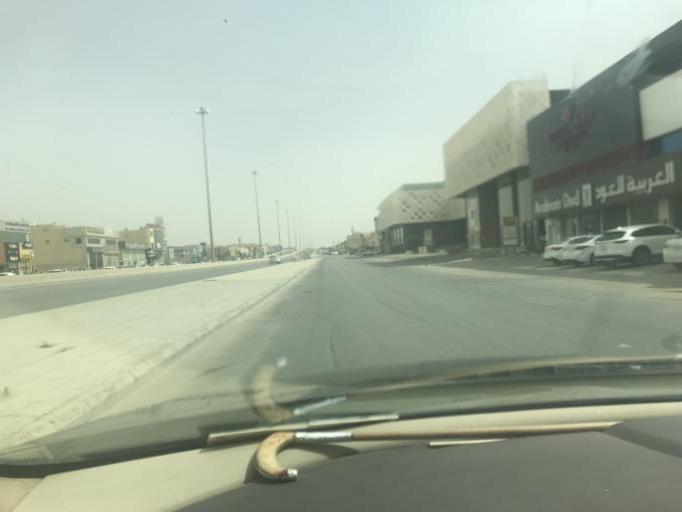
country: SA
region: Ar Riyad
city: Riyadh
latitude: 24.7967
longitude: 46.6982
